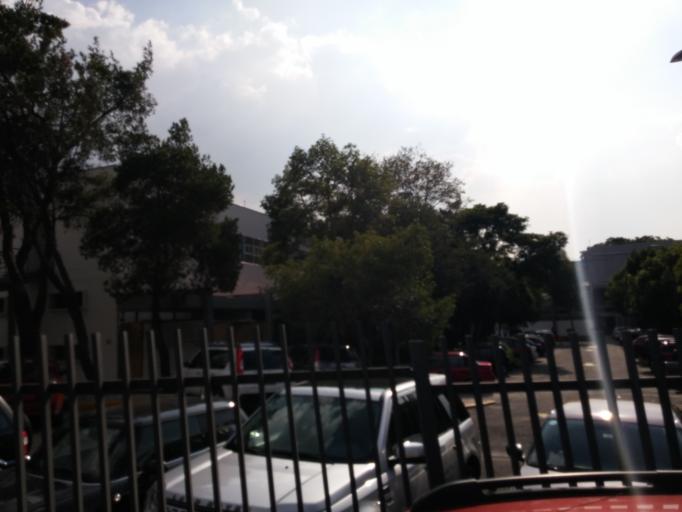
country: MX
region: Mexico City
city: Coyoacan
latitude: 19.3306
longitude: -99.1766
